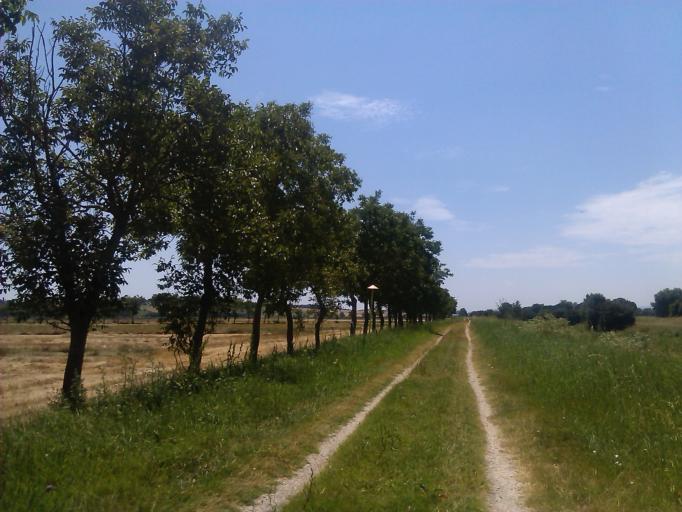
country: IT
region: Tuscany
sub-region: Province of Arezzo
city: Cesa
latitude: 43.3060
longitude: 11.8394
